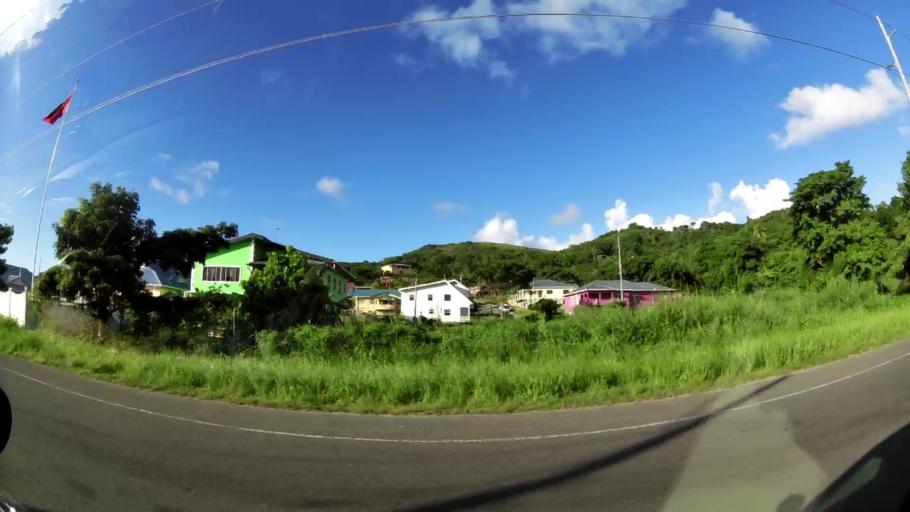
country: TT
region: Tobago
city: Scarborough
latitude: 11.1795
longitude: -60.7089
